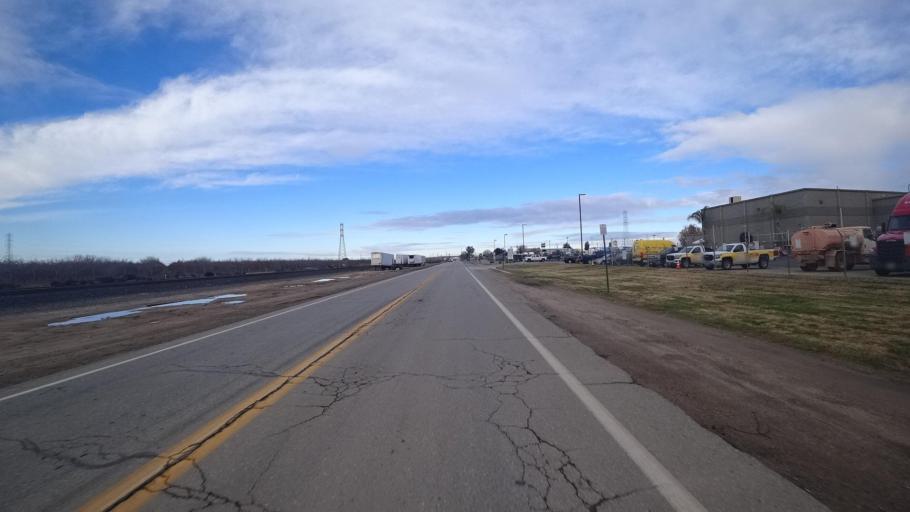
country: US
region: California
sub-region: Kern County
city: Greenacres
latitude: 35.4346
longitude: -119.0783
